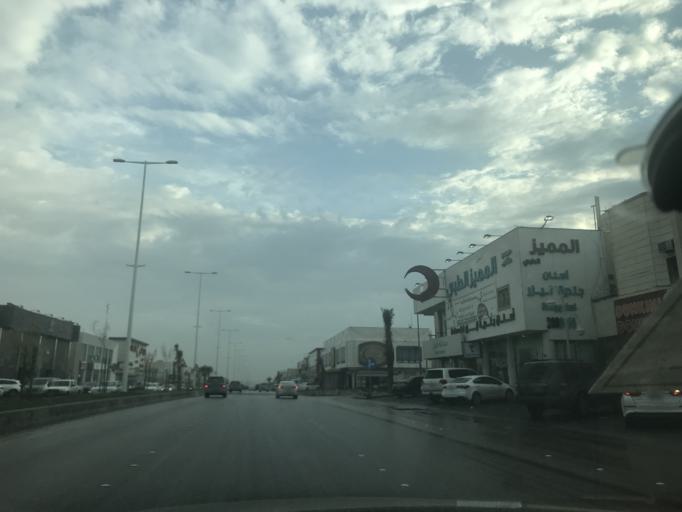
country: SA
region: Ar Riyad
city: Riyadh
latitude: 24.7412
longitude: 46.7513
